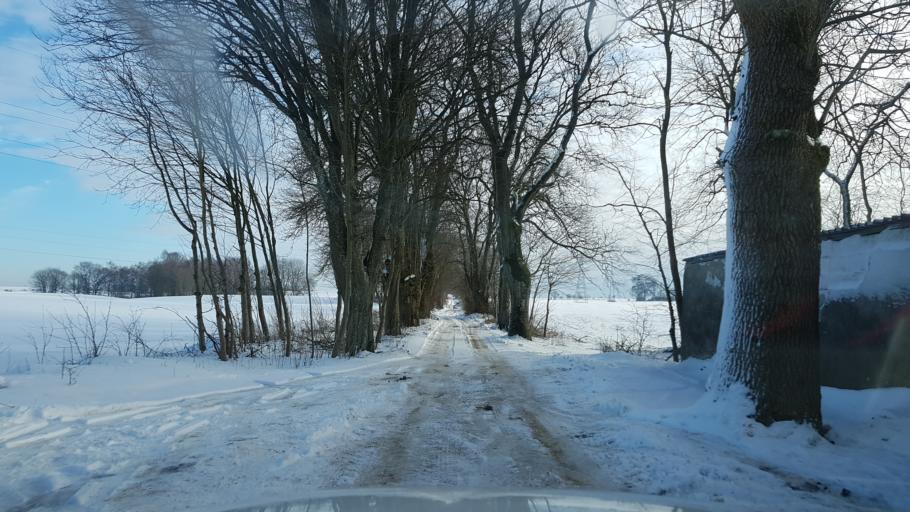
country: PL
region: West Pomeranian Voivodeship
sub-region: Powiat drawski
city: Drawsko Pomorskie
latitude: 53.5353
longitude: 15.7738
